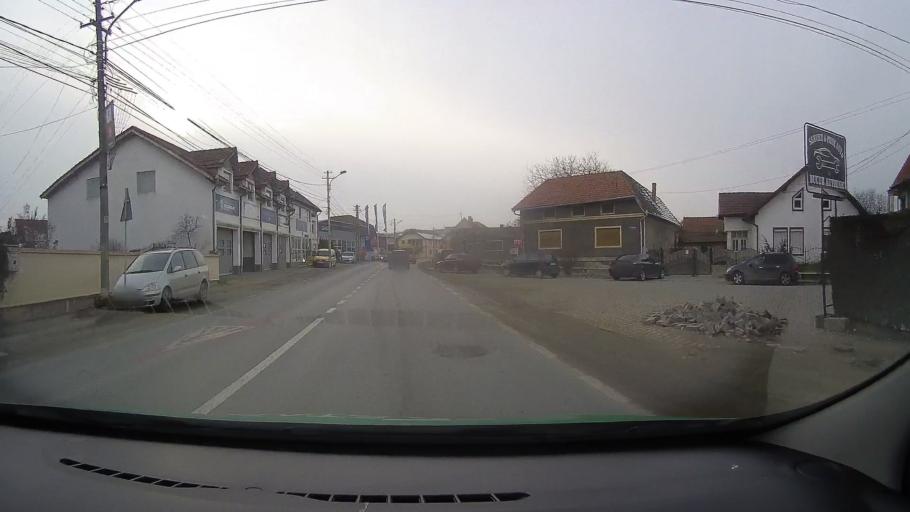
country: RO
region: Hunedoara
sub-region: Municipiul Orastie
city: Orastie
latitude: 45.8450
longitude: 23.2022
